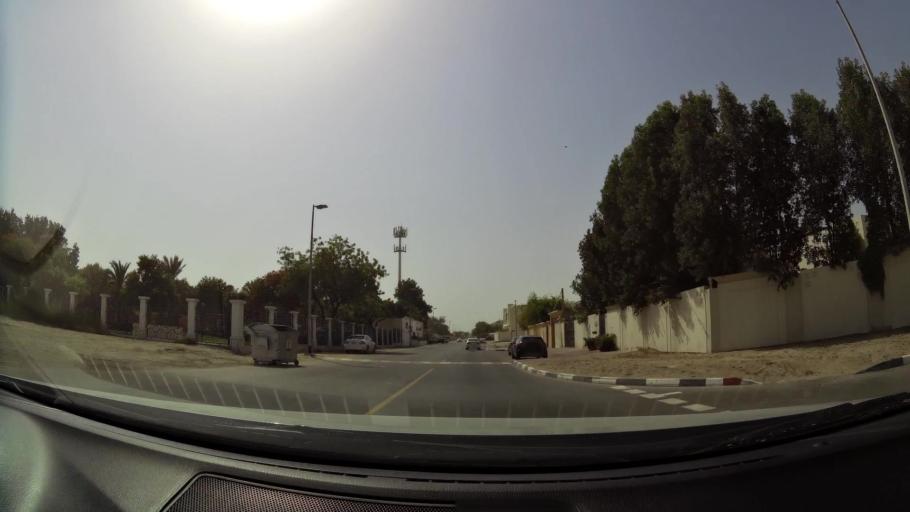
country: AE
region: Dubai
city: Dubai
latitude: 25.1689
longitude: 55.2575
